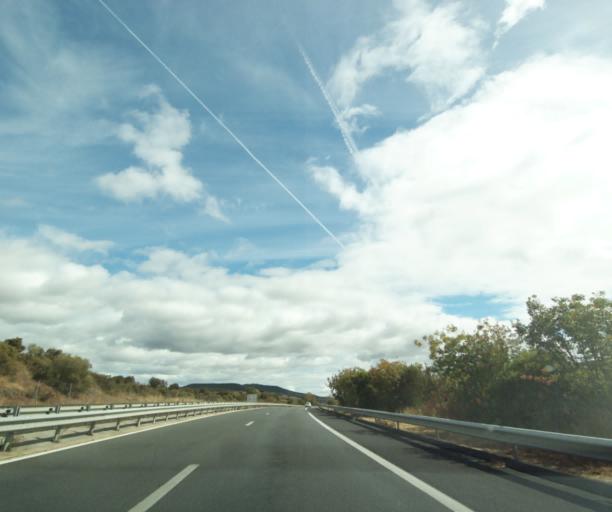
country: FR
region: Languedoc-Roussillon
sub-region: Departement de l'Herault
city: Lodeve
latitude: 43.6851
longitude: 3.3648
